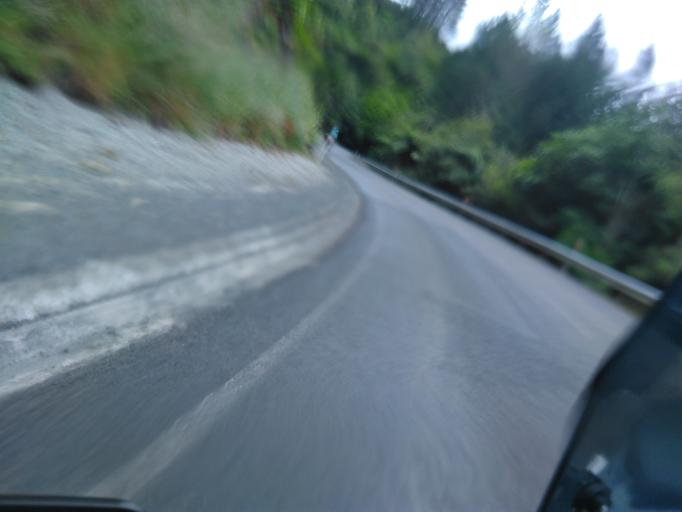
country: NZ
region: Bay of Plenty
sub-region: Opotiki District
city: Opotiki
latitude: -38.3452
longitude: 177.4503
